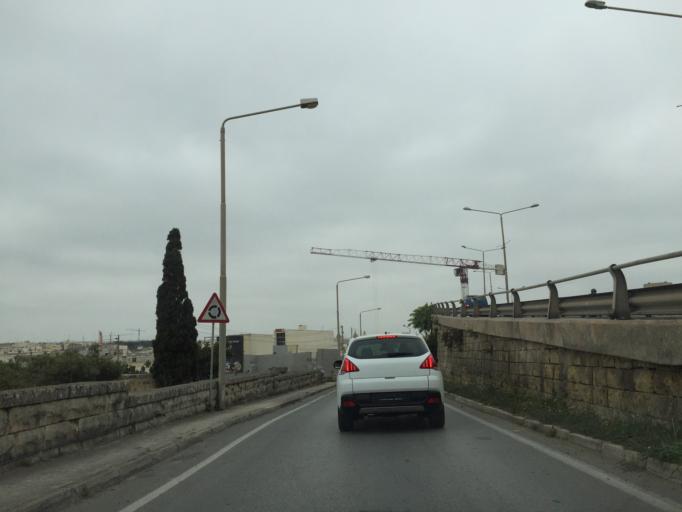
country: MT
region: Saint Venera
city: Santa Venera
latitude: 35.8839
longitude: 14.4751
